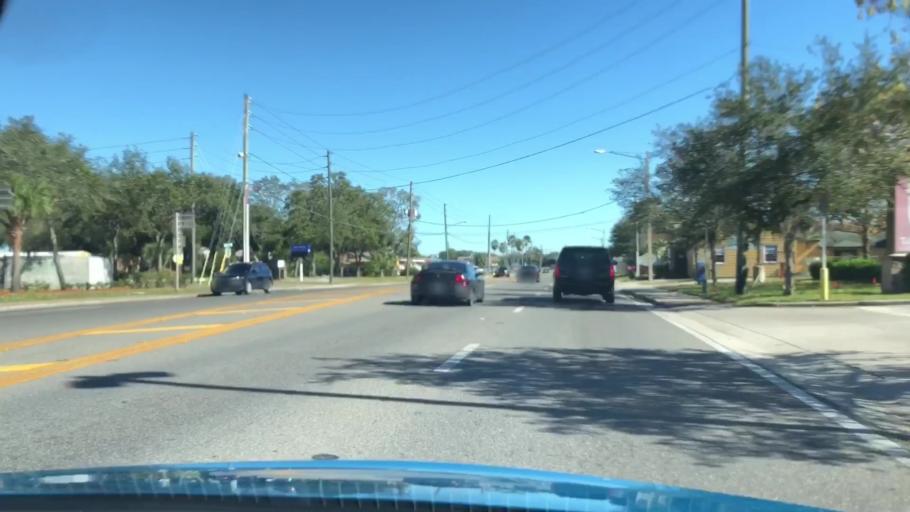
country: US
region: Florida
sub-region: Orange County
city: Sky Lake
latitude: 28.4724
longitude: -81.3958
